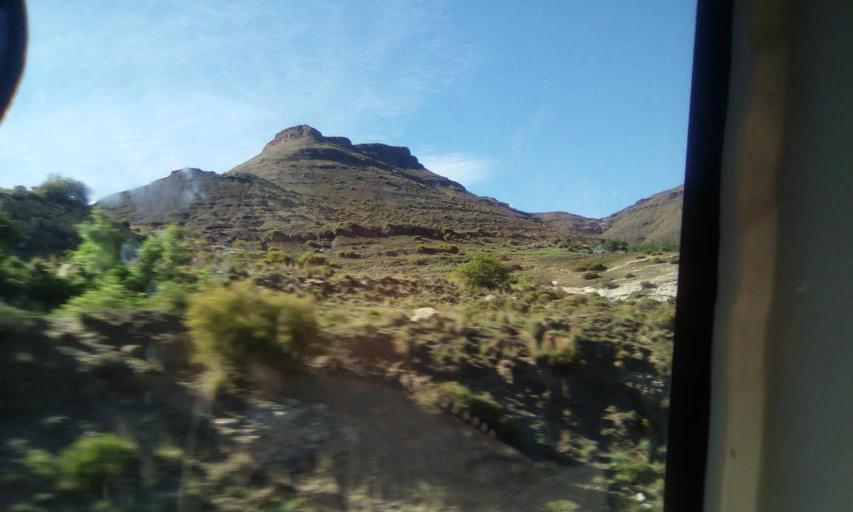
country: LS
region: Qacha's Nek
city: Qacha's Nek
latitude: -30.0555
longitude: 28.2944
